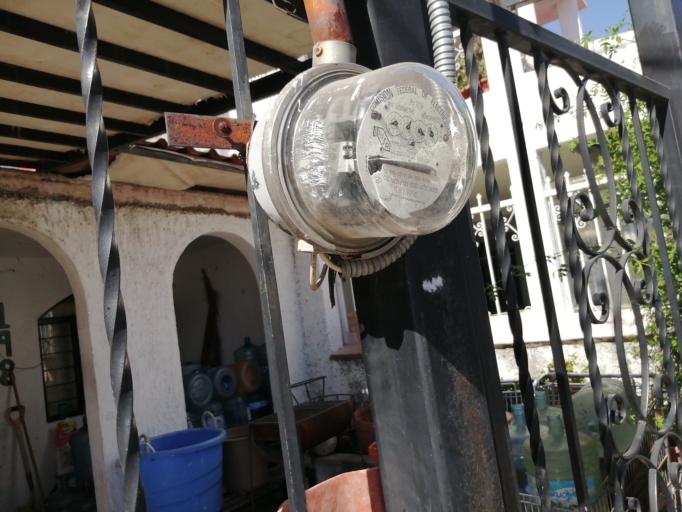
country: MX
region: Jalisco
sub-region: Zapopan
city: Zapopan
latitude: 20.7192
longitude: -103.3228
